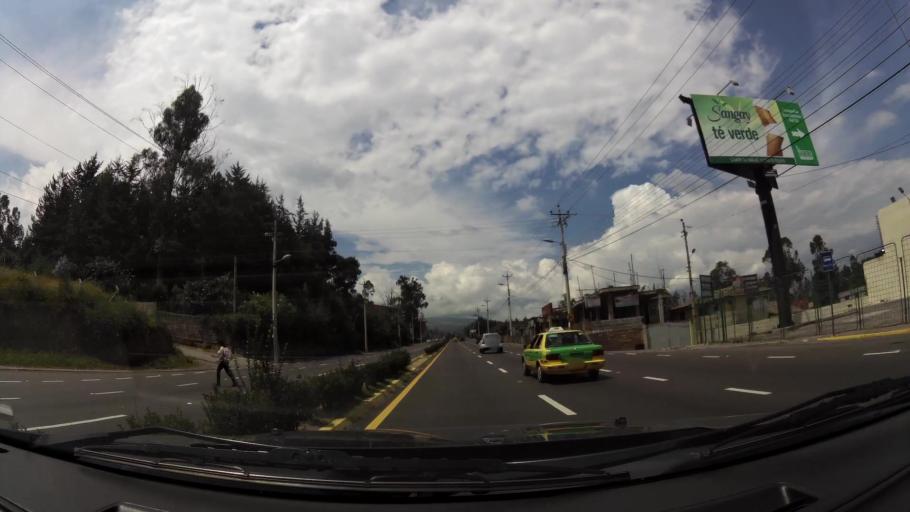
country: EC
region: Pichincha
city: Sangolqui
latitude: -0.2141
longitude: -78.3601
